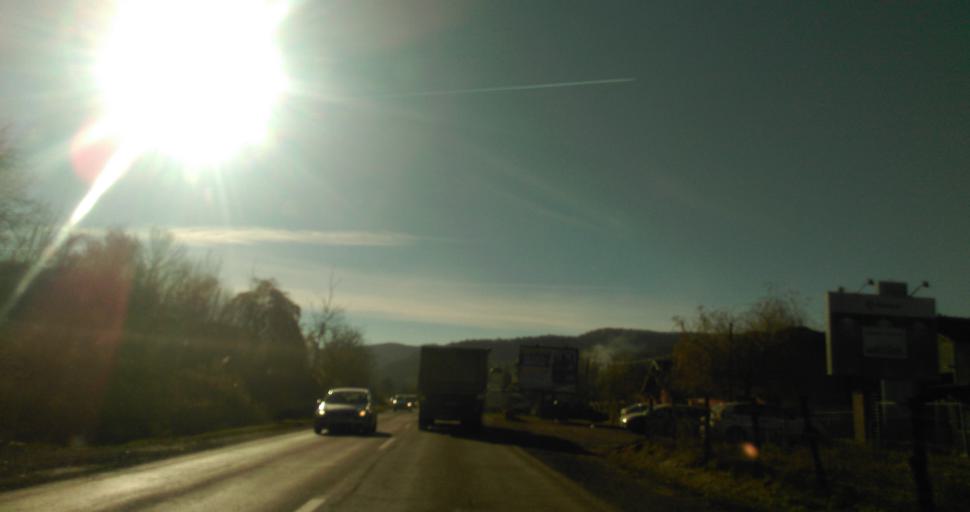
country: RS
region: Autonomna Pokrajina Vojvodina
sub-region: Juznobacki Okrug
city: Novi Sad
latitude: 45.1990
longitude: 19.8421
